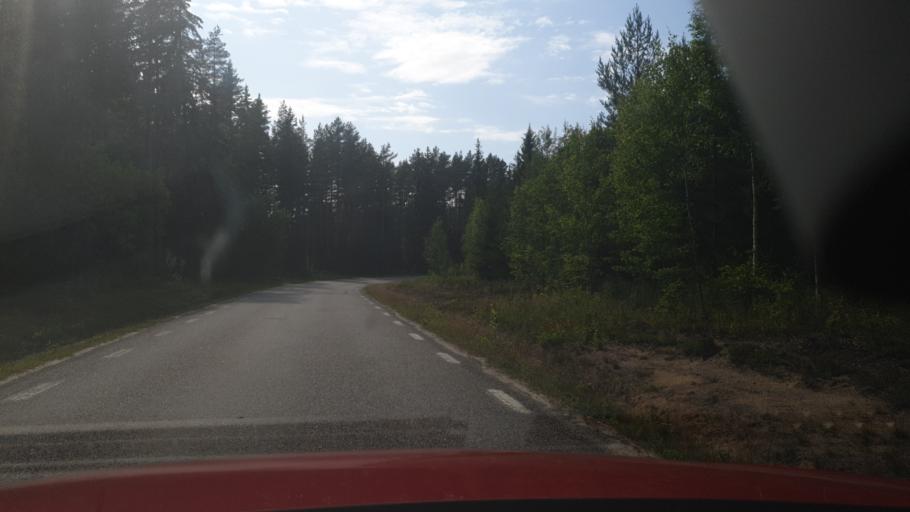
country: SE
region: Vaesternorrland
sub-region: Sundsvalls Kommun
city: Njurundabommen
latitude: 62.0361
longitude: 17.3687
